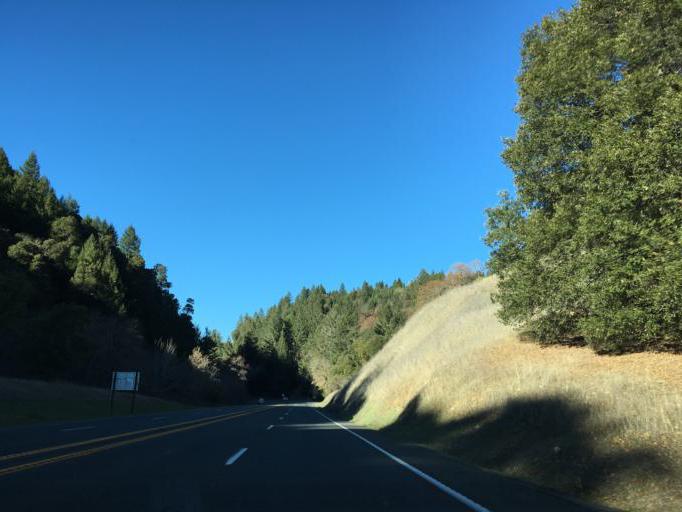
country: US
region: California
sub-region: Mendocino County
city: Laytonville
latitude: 39.5680
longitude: -123.4352
